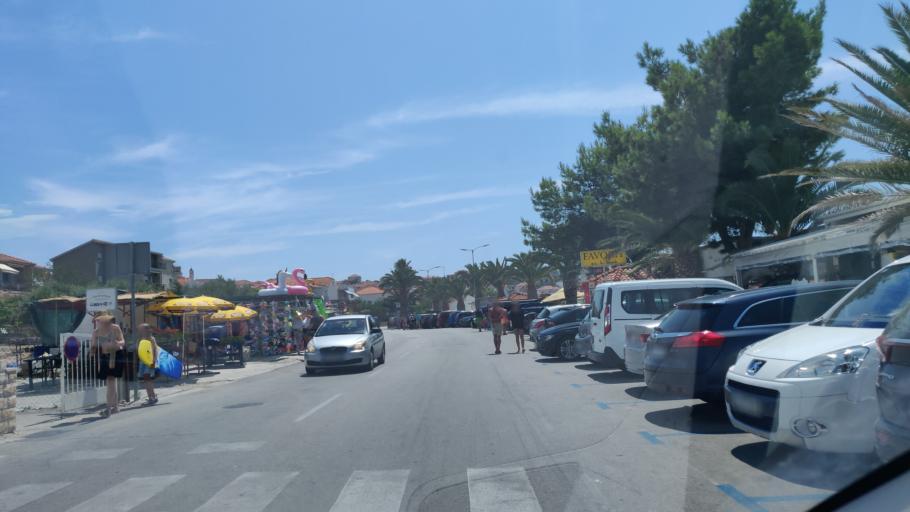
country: HR
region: Splitsko-Dalmatinska
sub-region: Grad Trogir
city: Trogir
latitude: 43.4990
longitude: 16.2602
